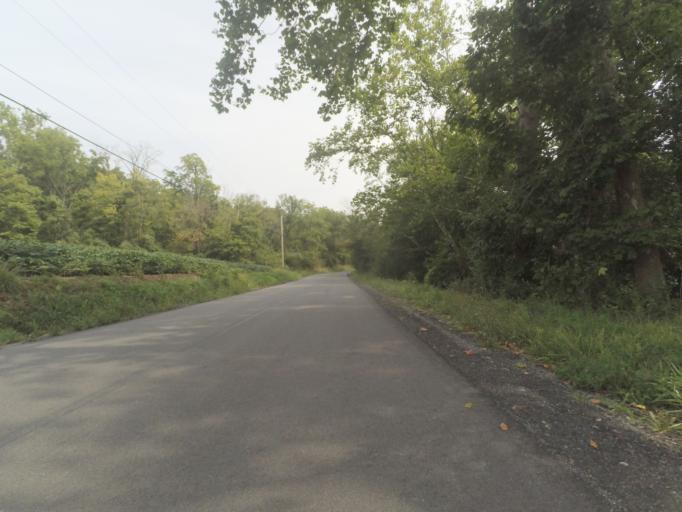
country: US
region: Pennsylvania
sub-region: Huntingdon County
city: Huntingdon
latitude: 40.5857
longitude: -78.0432
